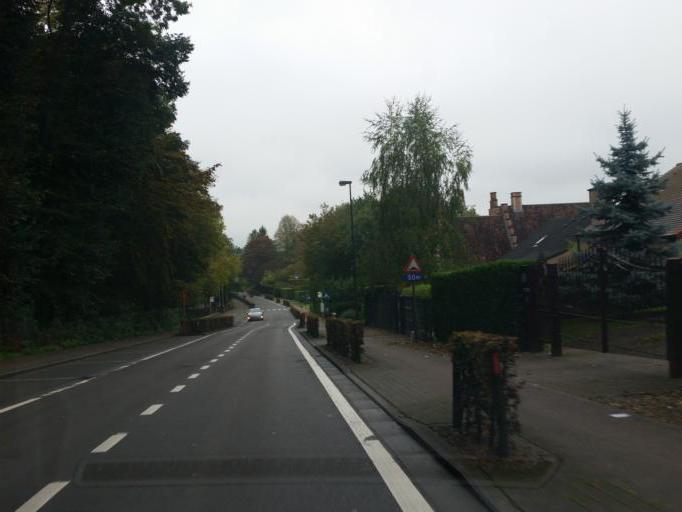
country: BE
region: Flanders
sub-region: Provincie Vlaams-Brabant
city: Sint-Pieters-Leeuw
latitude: 50.7804
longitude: 4.2510
